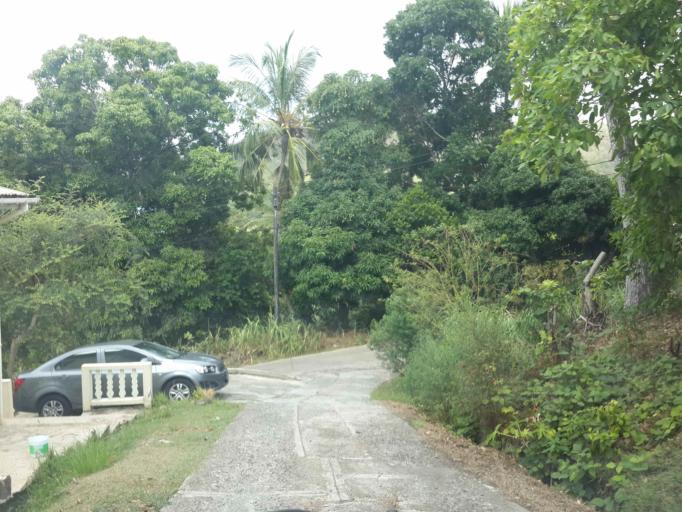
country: LC
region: Castries Quarter
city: Bisee
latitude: 14.0239
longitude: -60.9566
